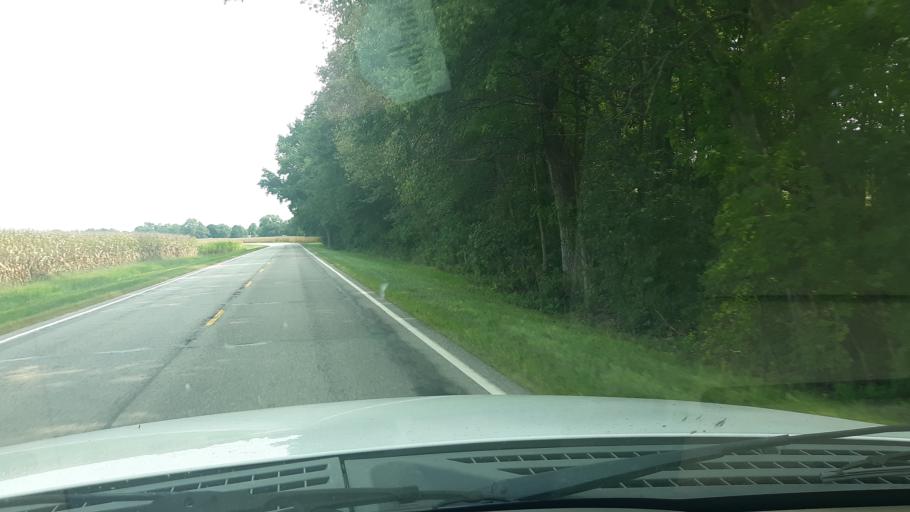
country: US
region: Illinois
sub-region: Edwards County
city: Grayville
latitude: 38.3047
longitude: -87.9463
